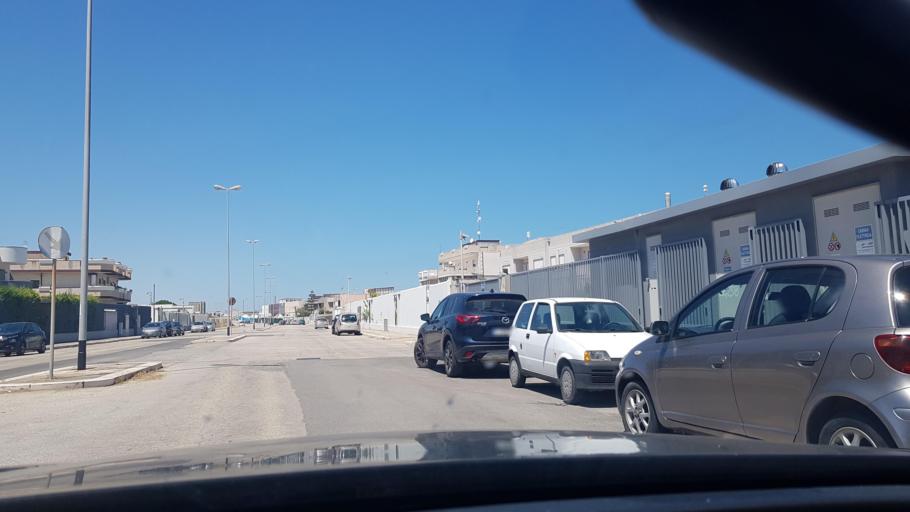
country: IT
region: Apulia
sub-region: Provincia di Barletta - Andria - Trani
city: Barletta
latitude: 41.3059
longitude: 16.3232
